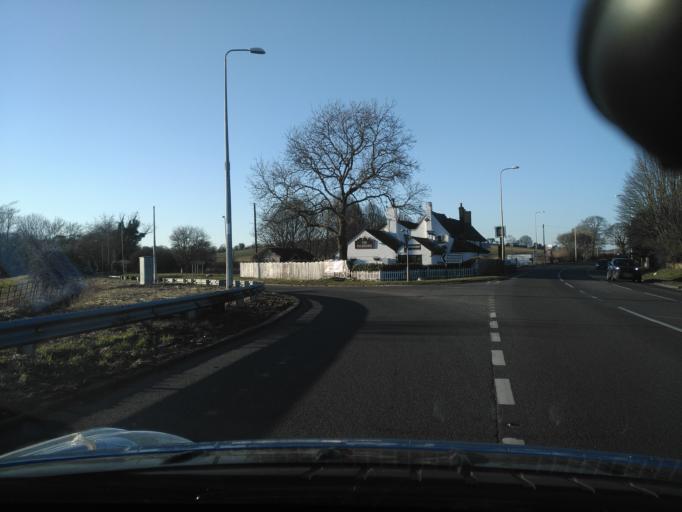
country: GB
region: England
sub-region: Hertfordshire
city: Markyate
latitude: 51.8498
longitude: -0.4767
